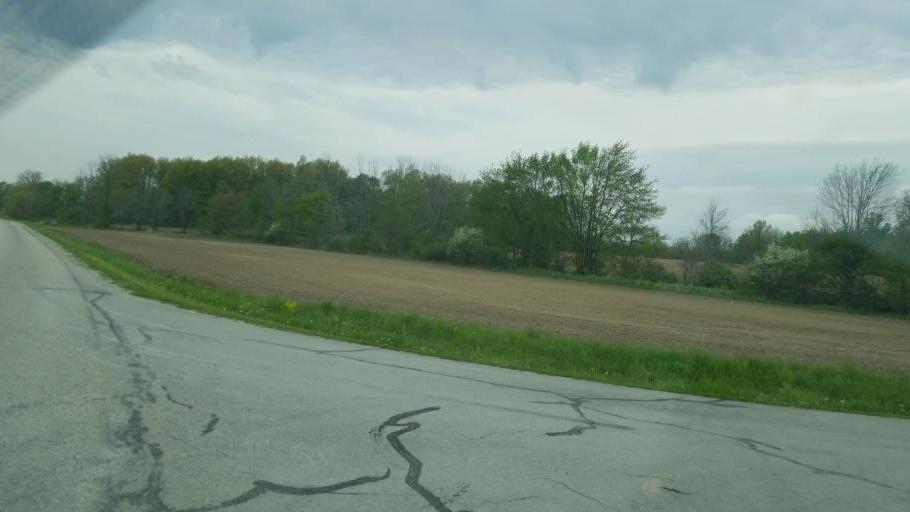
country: US
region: Ohio
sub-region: Huron County
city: Willard
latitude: 41.0081
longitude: -82.8383
